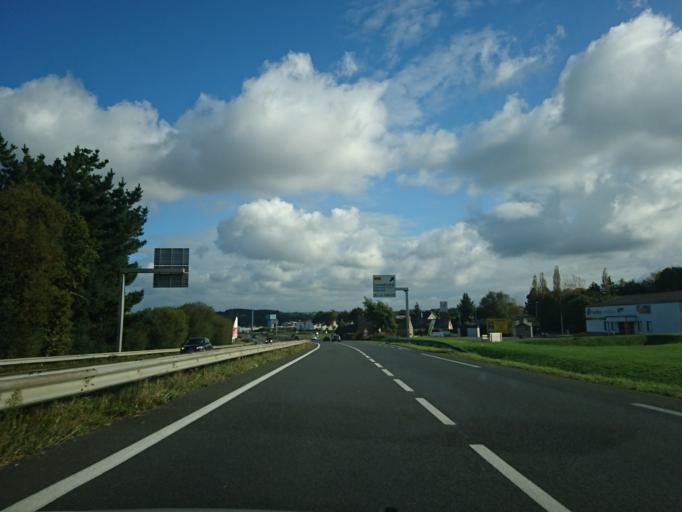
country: FR
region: Brittany
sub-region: Departement des Cotes-d'Armor
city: Graces
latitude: 48.5513
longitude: -3.1689
